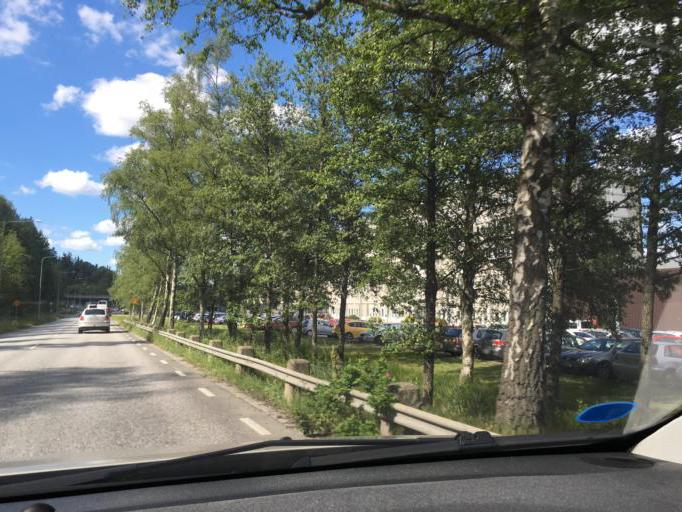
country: SE
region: Stockholm
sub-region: Sodertalje Kommun
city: Soedertaelje
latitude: 59.1732
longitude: 17.6357
